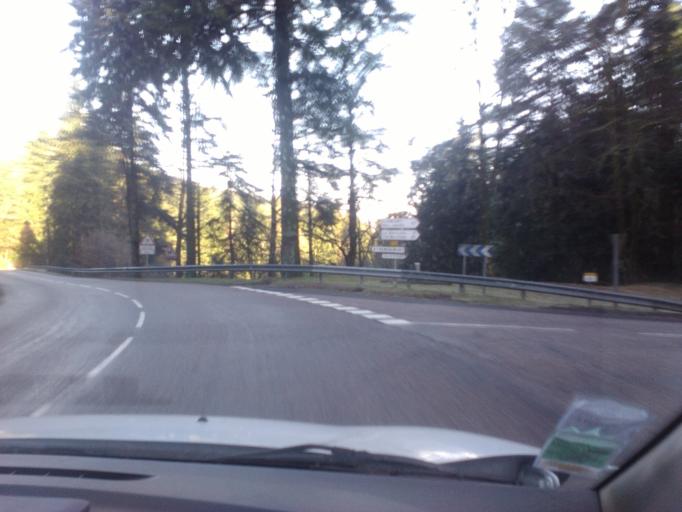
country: FR
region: Lorraine
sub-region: Departement des Vosges
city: Remiremont
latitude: 47.9939
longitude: 6.5723
